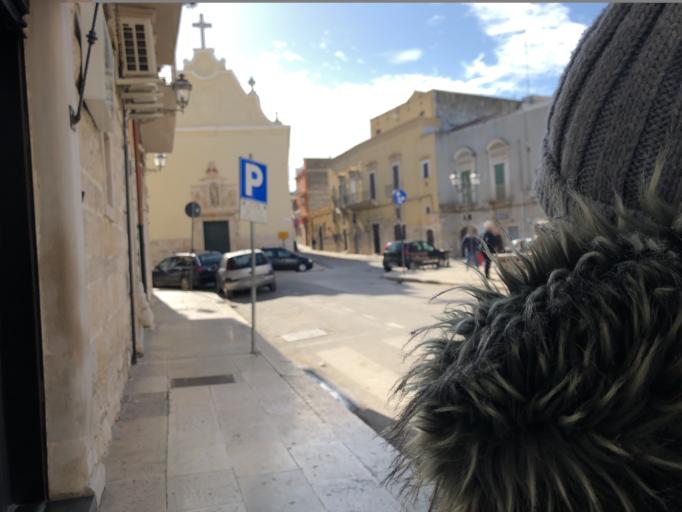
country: IT
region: Apulia
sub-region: Provincia di Barletta - Andria - Trani
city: Andria
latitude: 41.2233
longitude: 16.2935
